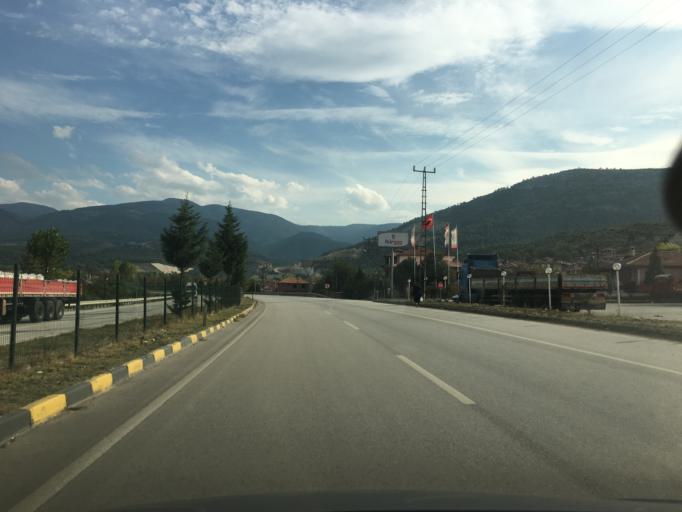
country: TR
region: Karabuk
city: Karabuk
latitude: 41.1039
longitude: 32.6690
